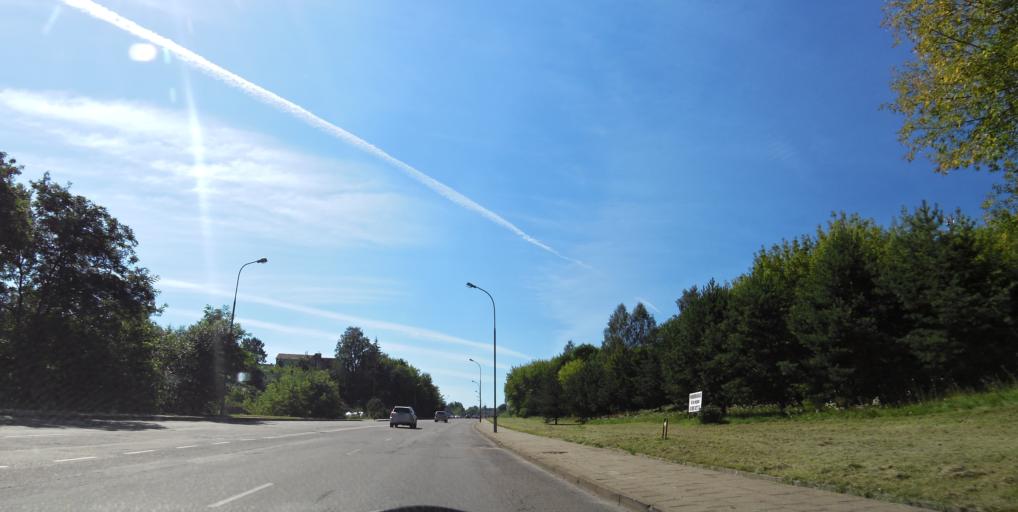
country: LT
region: Vilnius County
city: Rasos
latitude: 54.6652
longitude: 25.3051
